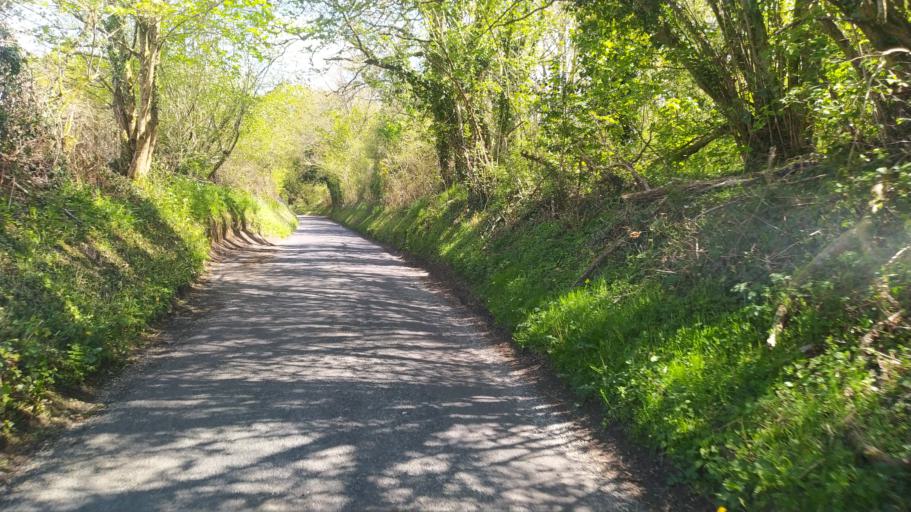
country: GB
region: England
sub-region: Dorset
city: Alderholt
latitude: 50.8939
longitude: -1.8092
